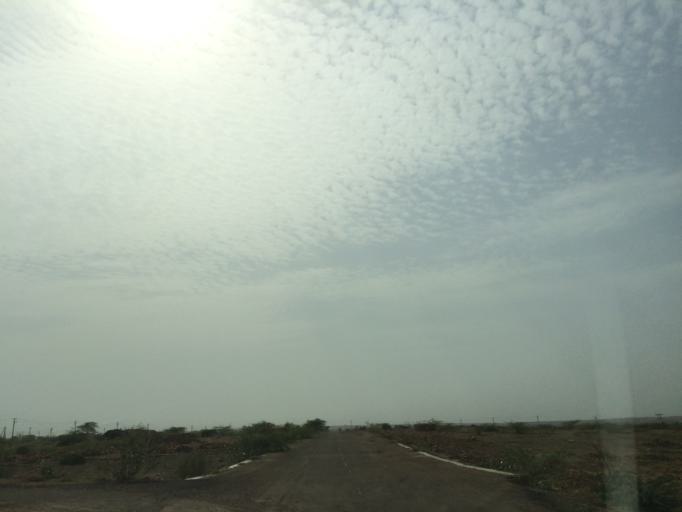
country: IN
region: Rajasthan
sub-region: Jaisalmer
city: Jaisalmer
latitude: 26.8738
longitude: 70.8983
